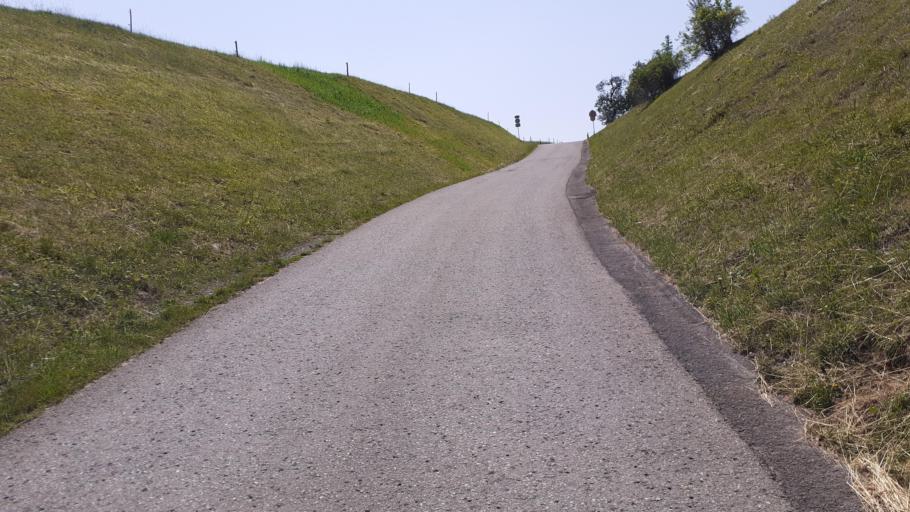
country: AT
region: Vorarlberg
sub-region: Politischer Bezirk Bregenz
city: Doren
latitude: 47.4660
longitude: 9.8527
